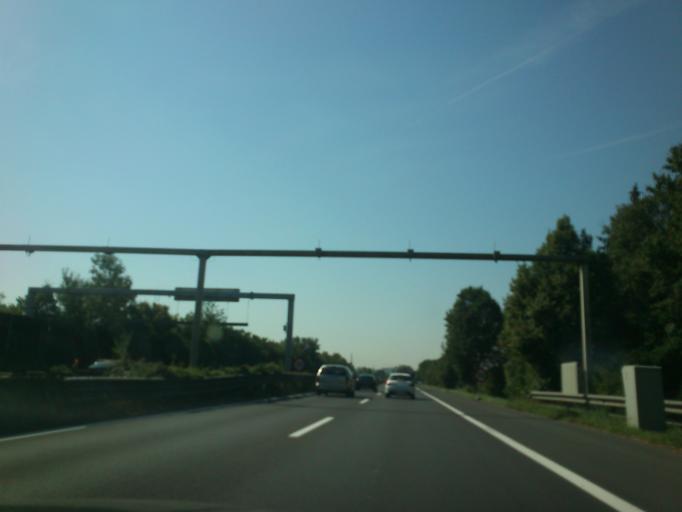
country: AT
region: Upper Austria
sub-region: Politischer Bezirk Linz-Land
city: Ansfelden
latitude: 48.2506
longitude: 14.2971
